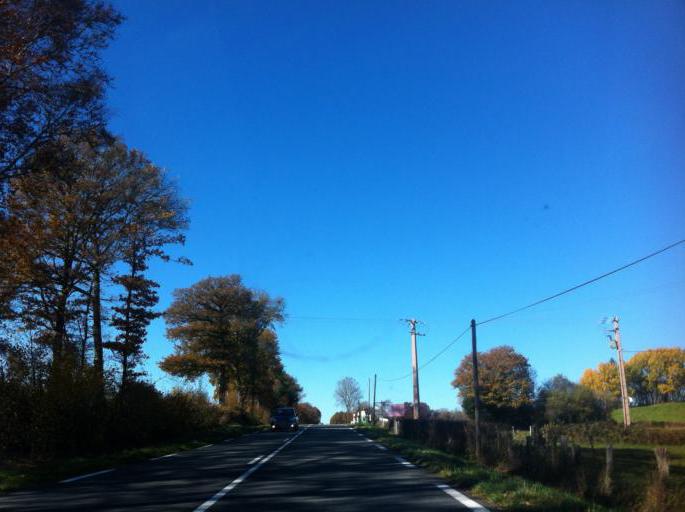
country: FR
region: Limousin
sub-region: Departement de la Creuse
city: Auzances
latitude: 45.8596
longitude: 2.5903
